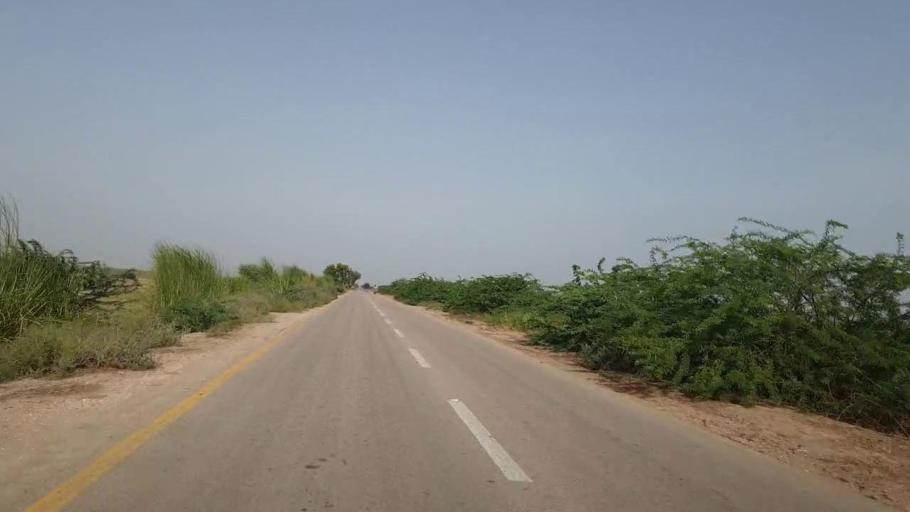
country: PK
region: Sindh
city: Bandhi
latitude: 26.5876
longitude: 68.2303
